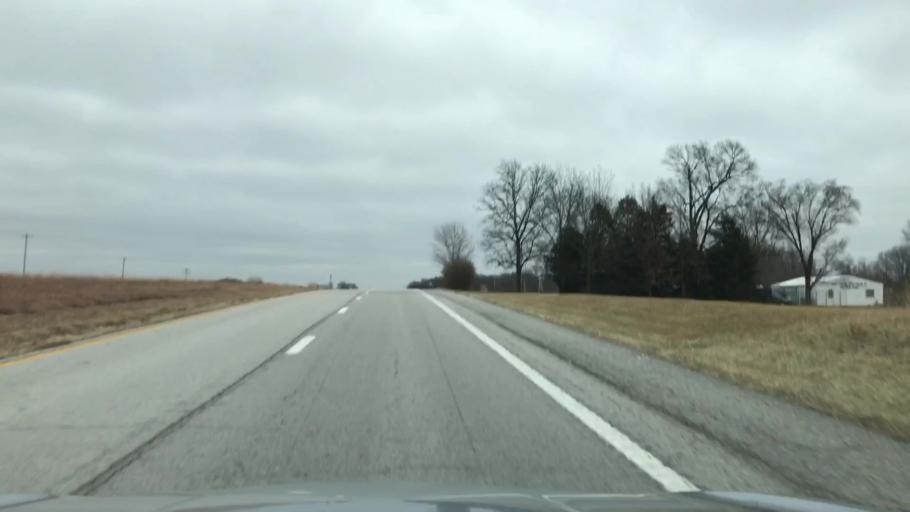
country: US
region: Missouri
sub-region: Linn County
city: Linneus
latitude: 39.7776
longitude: -93.2740
